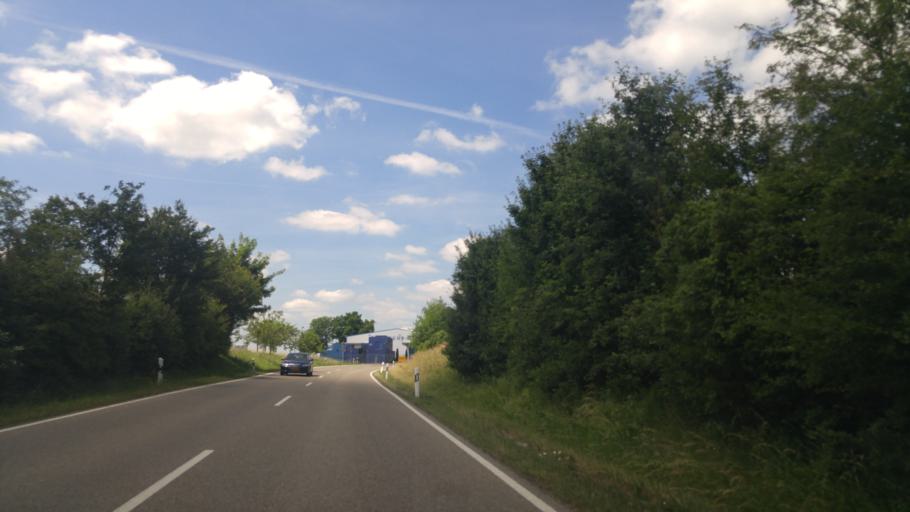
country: DE
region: Bavaria
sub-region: Regierungsbezirk Mittelfranken
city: Steinsfeld
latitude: 49.4400
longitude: 10.2166
